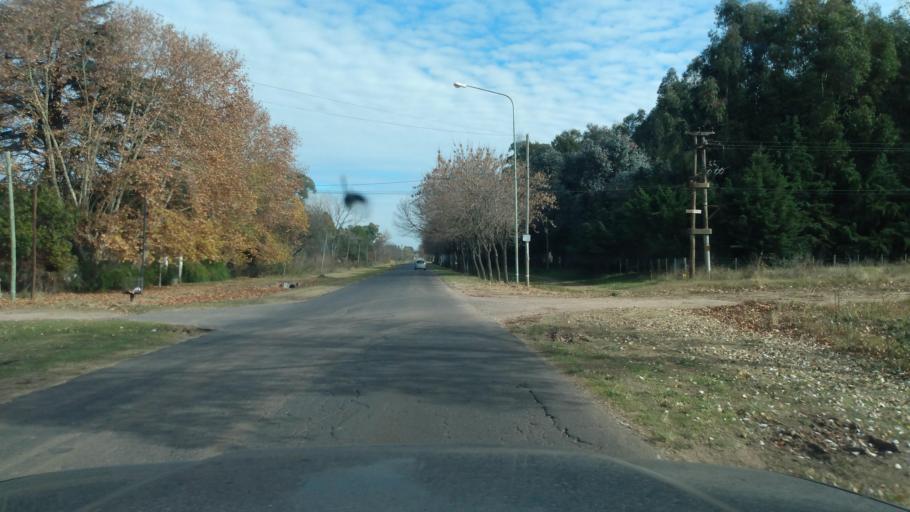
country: AR
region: Buenos Aires
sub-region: Partido de Lujan
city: Lujan
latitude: -34.5725
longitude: -59.1575
